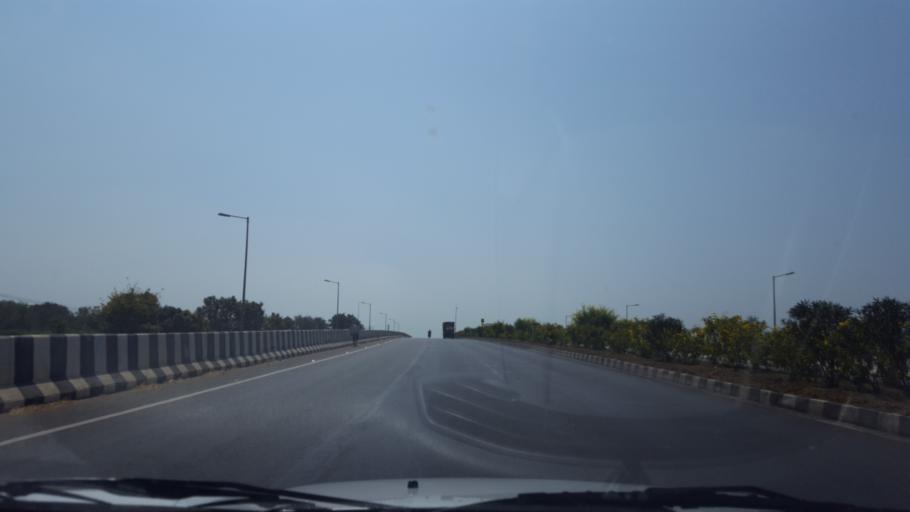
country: IN
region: Andhra Pradesh
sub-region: Prakasam
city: Ongole
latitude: 15.6592
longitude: 80.0152
